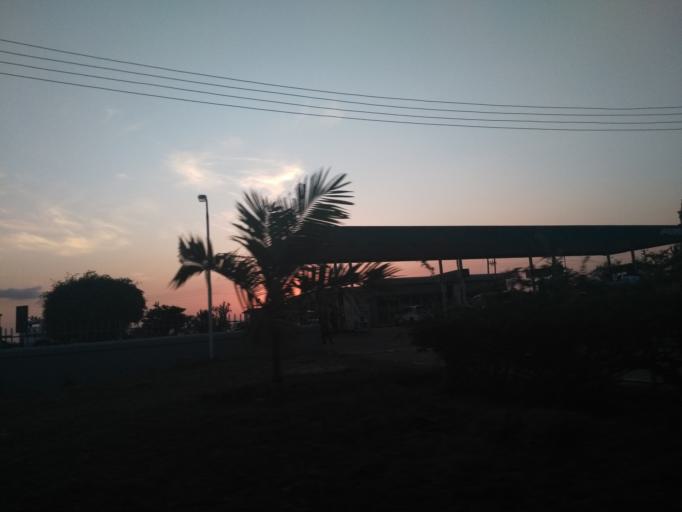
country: TZ
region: Dar es Salaam
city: Dar es Salaam
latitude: -6.8639
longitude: 39.2063
